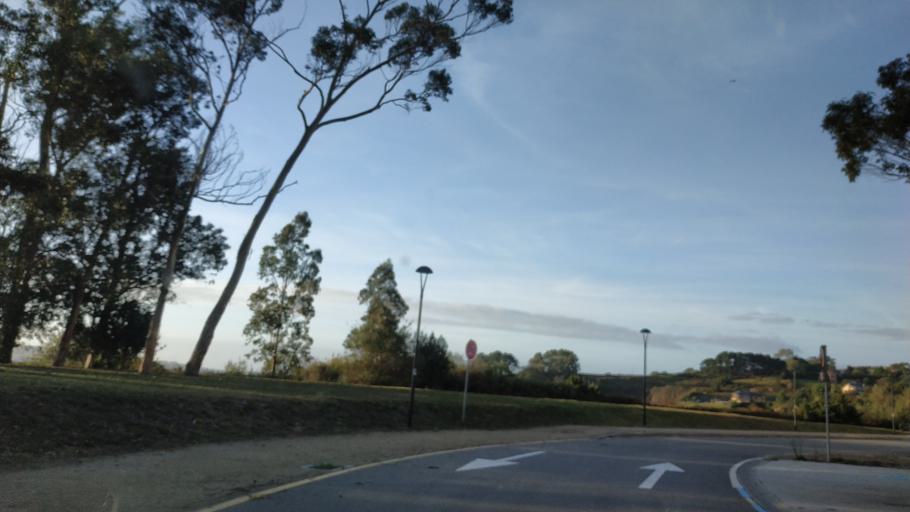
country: ES
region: Galicia
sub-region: Provincia da Coruna
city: Oleiros
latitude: 43.3511
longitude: -8.3478
